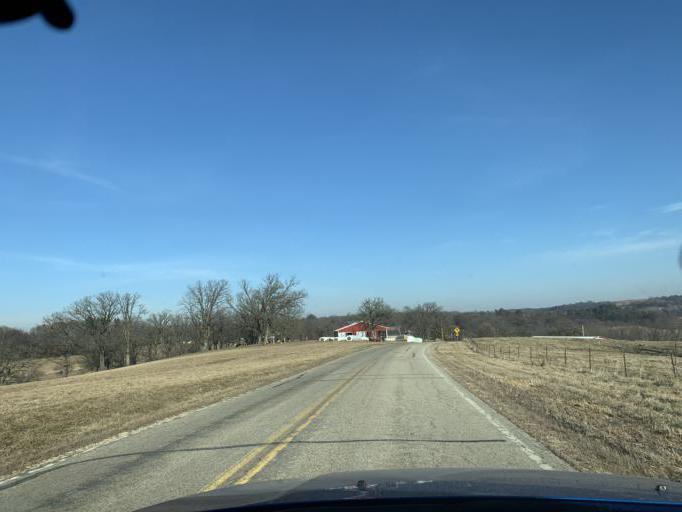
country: US
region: Wisconsin
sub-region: Iowa County
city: Barneveld
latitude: 42.8658
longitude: -89.9363
